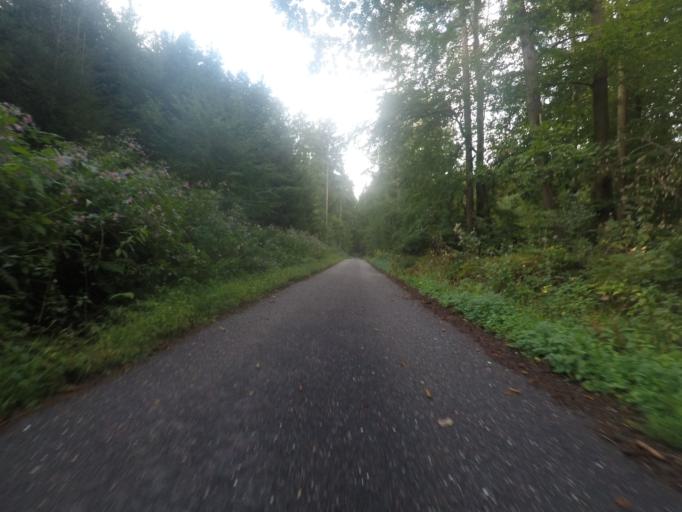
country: DE
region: Baden-Wuerttemberg
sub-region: Karlsruhe Region
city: Ettlingen
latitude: 48.8917
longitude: 8.4039
